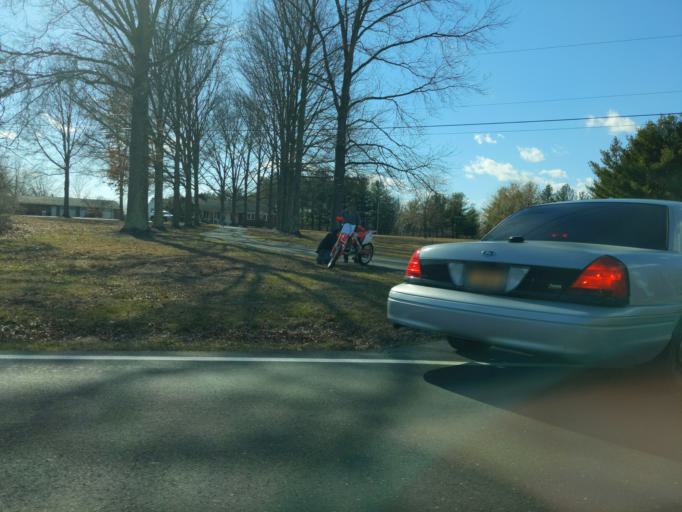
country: US
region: Pennsylvania
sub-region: Montgomery County
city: Pennsburg
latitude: 40.3958
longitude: -75.4696
